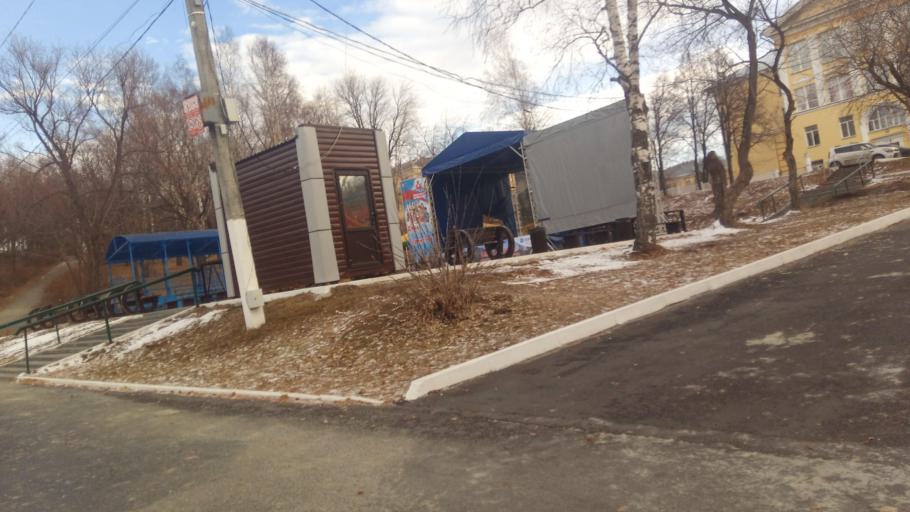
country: RU
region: Chelyabinsk
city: Zlatoust
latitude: 55.1083
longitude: 59.7204
